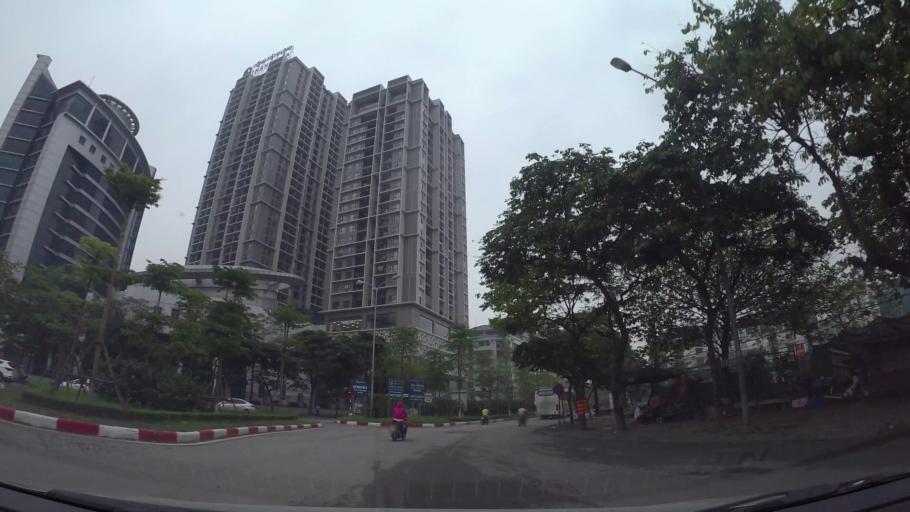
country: VN
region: Ha Noi
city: Cau Giay
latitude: 21.0277
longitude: 105.7871
